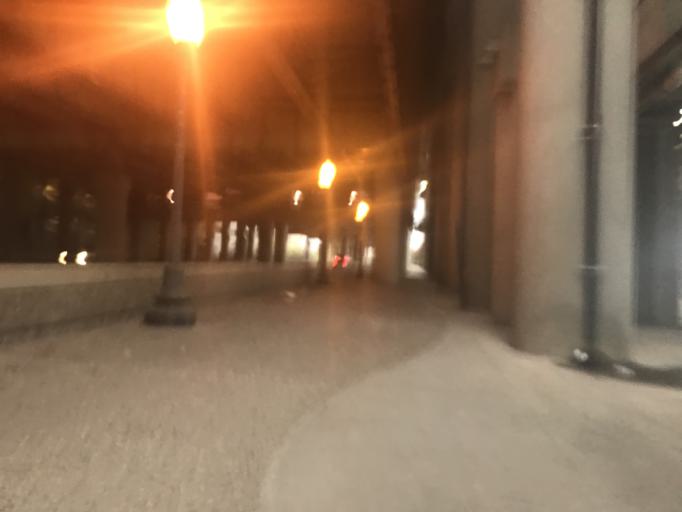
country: US
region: Kentucky
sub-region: Jefferson County
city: Louisville
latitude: 38.2590
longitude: -85.7568
